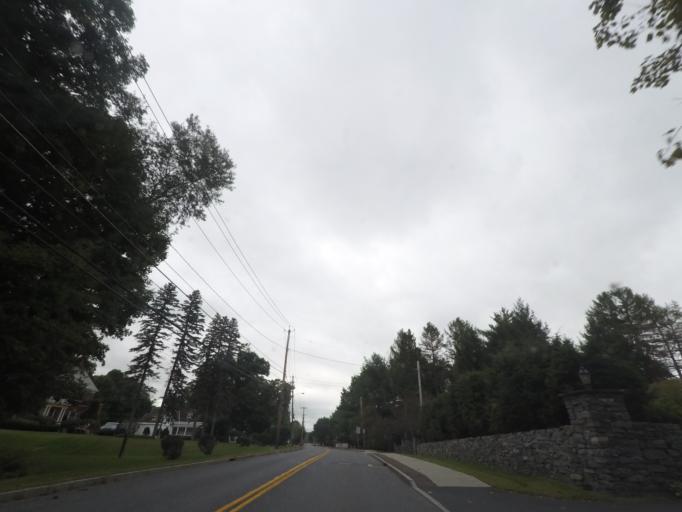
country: US
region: New York
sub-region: Rensselaer County
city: Hoosick Falls
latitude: 42.9098
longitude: -73.3514
